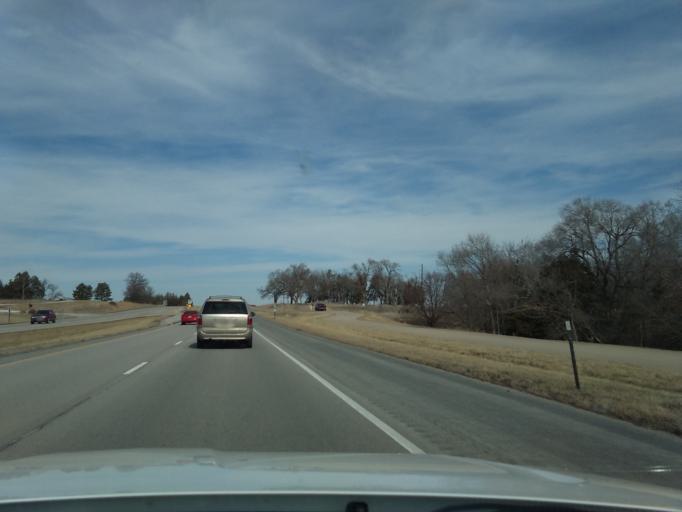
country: US
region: Nebraska
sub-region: Lancaster County
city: Hickman
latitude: 40.6745
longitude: -96.7050
